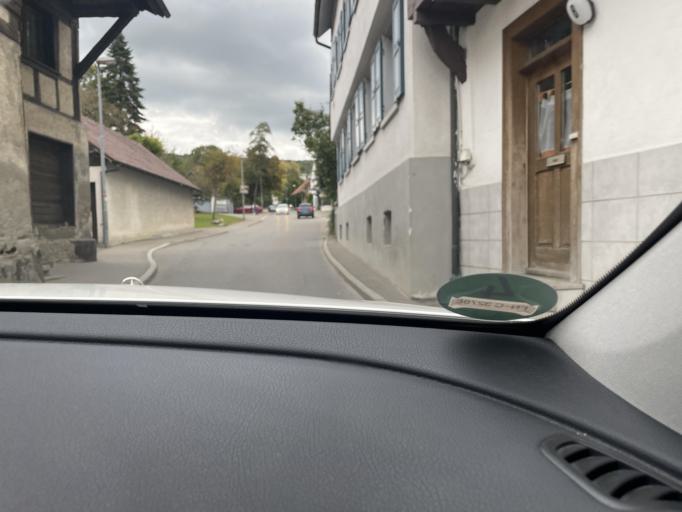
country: DE
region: Baden-Wuerttemberg
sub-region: Tuebingen Region
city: Markdorf
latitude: 47.7218
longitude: 9.3927
